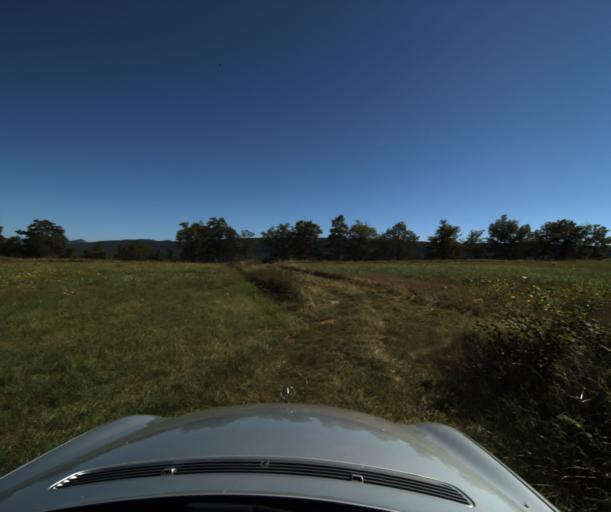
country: FR
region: Midi-Pyrenees
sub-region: Departement de l'Ariege
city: Belesta
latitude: 42.9643
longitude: 1.9238
